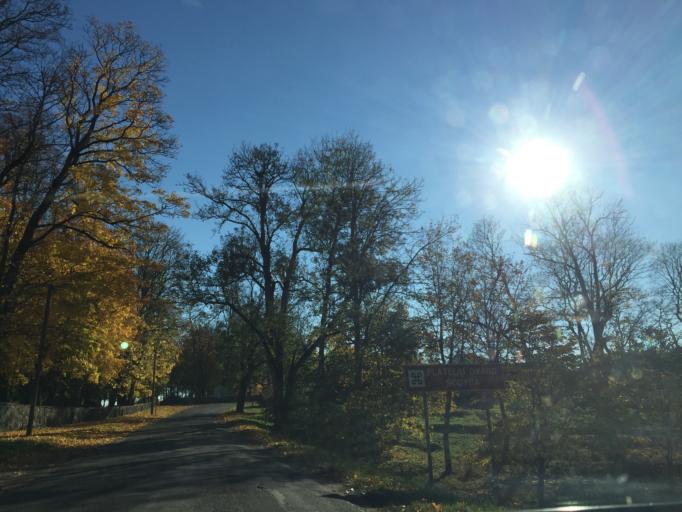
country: LT
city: Plateliai
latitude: 56.0401
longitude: 21.8155
